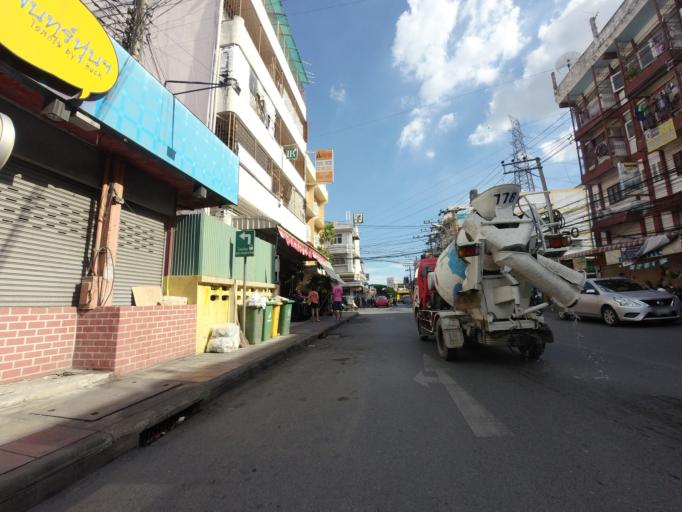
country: TH
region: Bangkok
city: Huai Khwang
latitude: 13.7788
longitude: 100.5844
